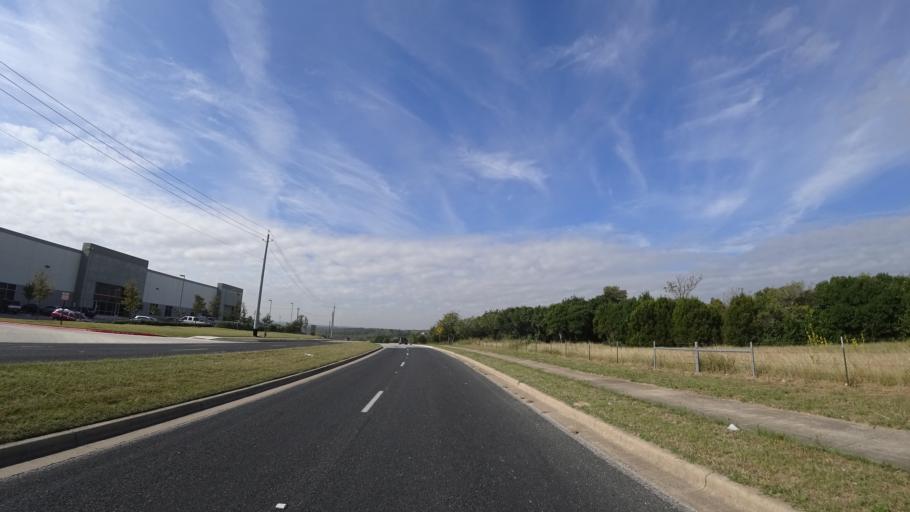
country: US
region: Texas
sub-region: Travis County
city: Austin
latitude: 30.2018
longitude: -97.7209
